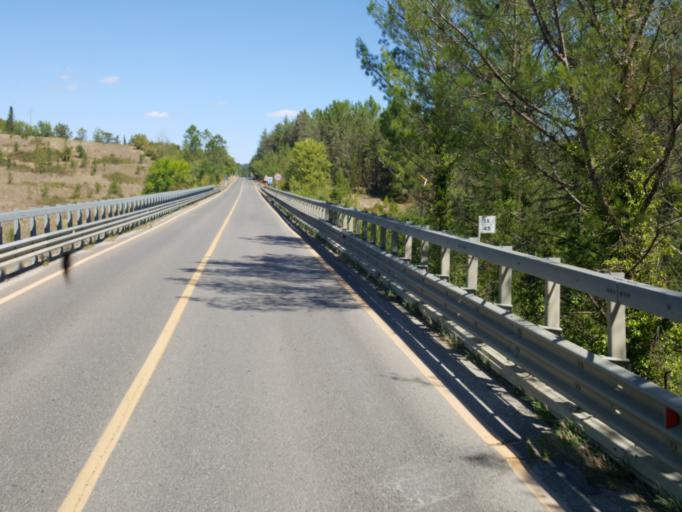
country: IT
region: Tuscany
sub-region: Provincia di Siena
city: Murlo
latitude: 43.1204
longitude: 11.2968
